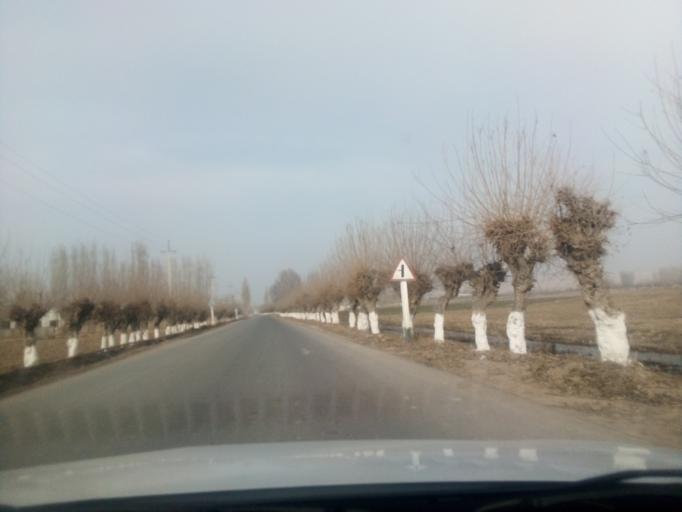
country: UZ
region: Namangan
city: Pop Shahri
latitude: 40.9744
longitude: 71.0997
